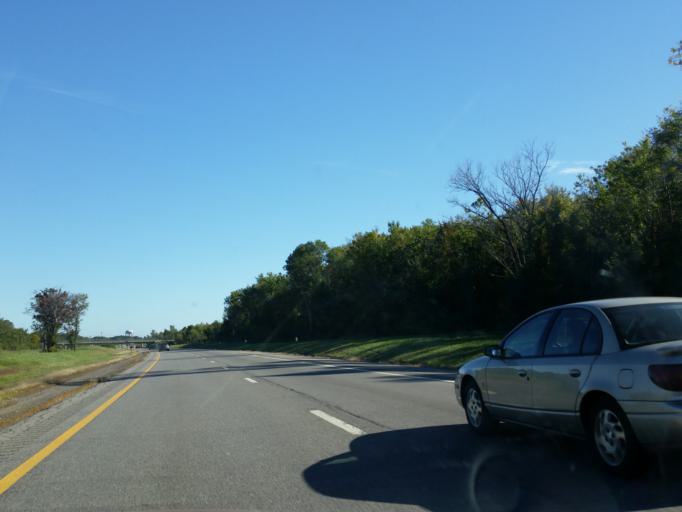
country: US
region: New York
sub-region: Erie County
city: Hamburg
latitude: 42.7464
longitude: -78.8369
